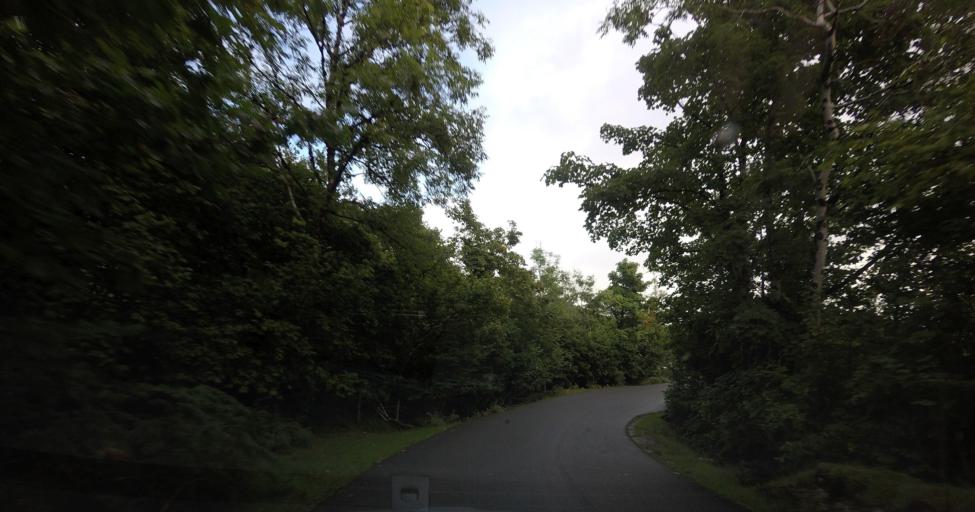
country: GB
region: Scotland
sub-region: Highland
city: Portree
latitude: 57.2118
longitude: -5.9940
